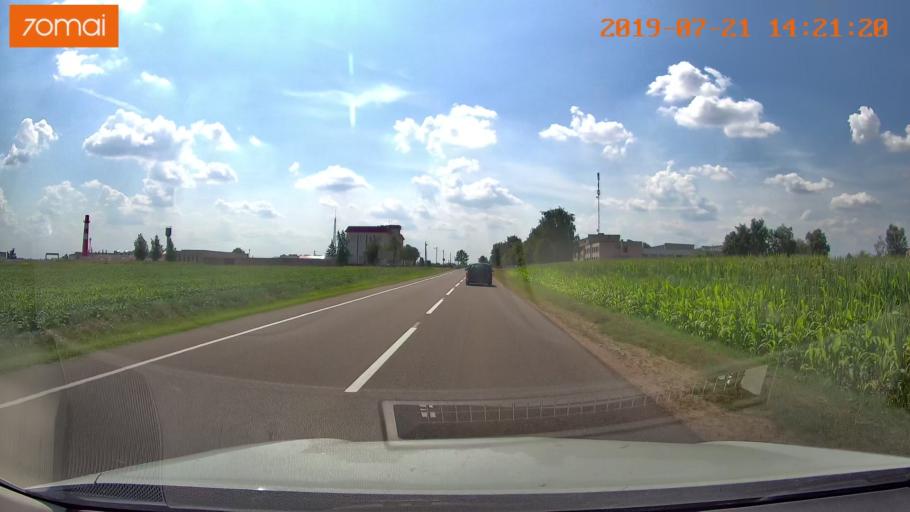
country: BY
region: Grodnenskaya
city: Karelichy
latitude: 53.5771
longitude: 26.1462
